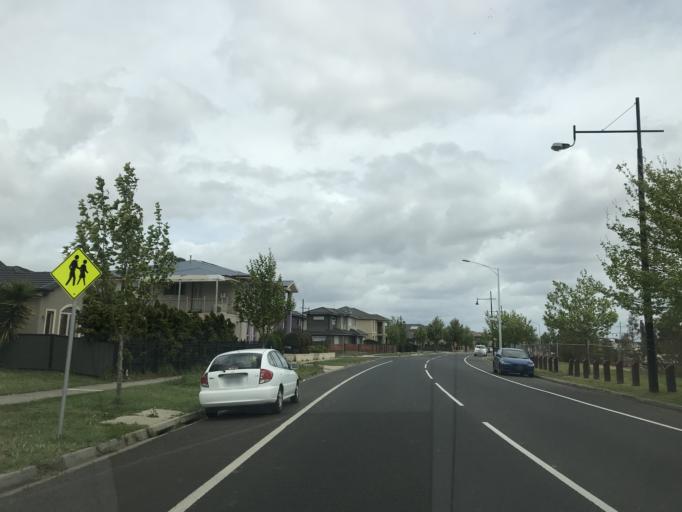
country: AU
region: Victoria
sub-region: Brimbank
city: Derrimut
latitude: -37.7928
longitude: 144.7664
